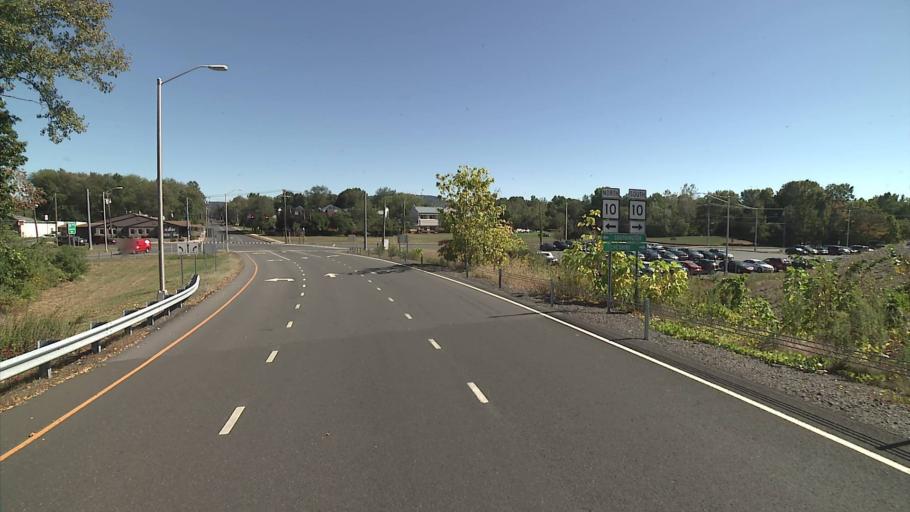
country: US
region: Connecticut
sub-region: New Haven County
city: Cheshire Village
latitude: 41.5736
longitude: -72.8969
